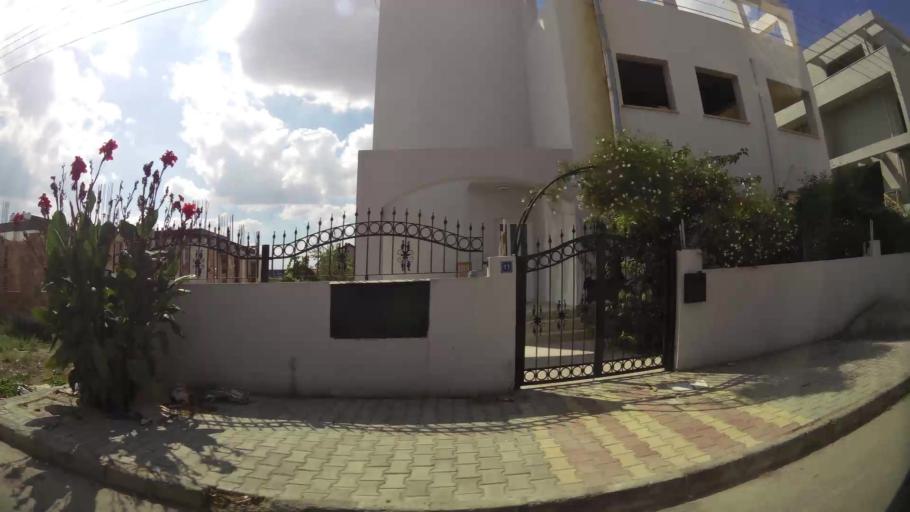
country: CY
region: Lefkosia
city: Nicosia
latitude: 35.2200
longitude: 33.2961
